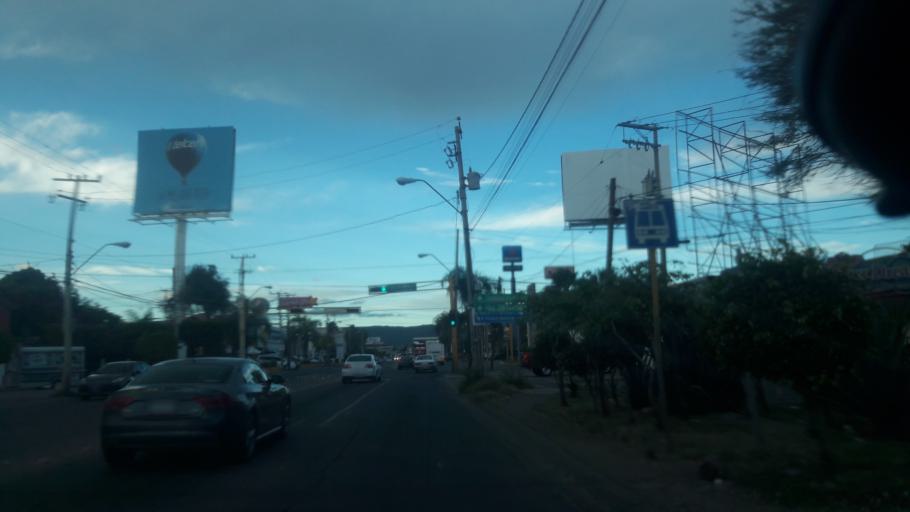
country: MX
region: Guanajuato
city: Leon
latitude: 21.1523
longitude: -101.6891
